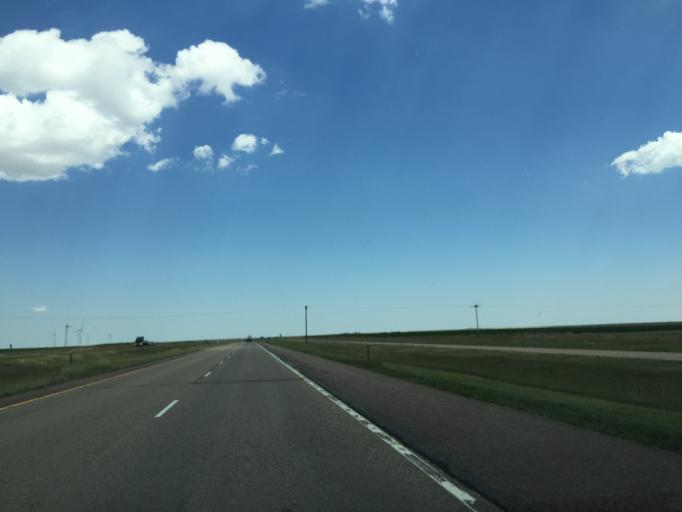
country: US
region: Colorado
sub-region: Lincoln County
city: Hugo
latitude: 39.2782
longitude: -103.4275
